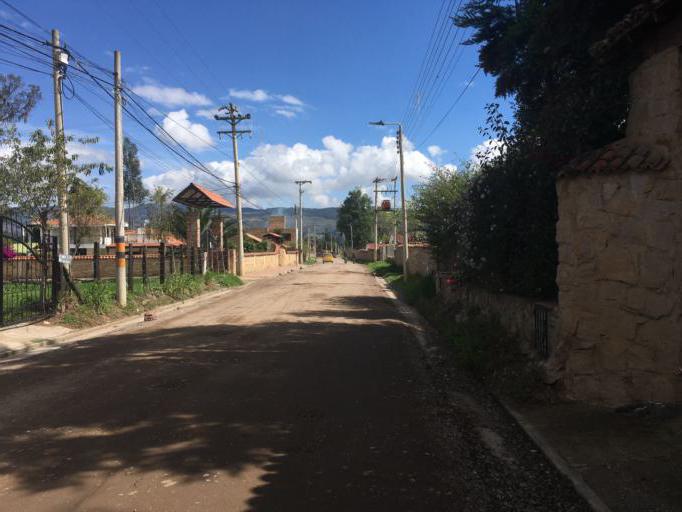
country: CO
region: Boyaca
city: Firavitoba
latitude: 5.6644
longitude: -72.9602
